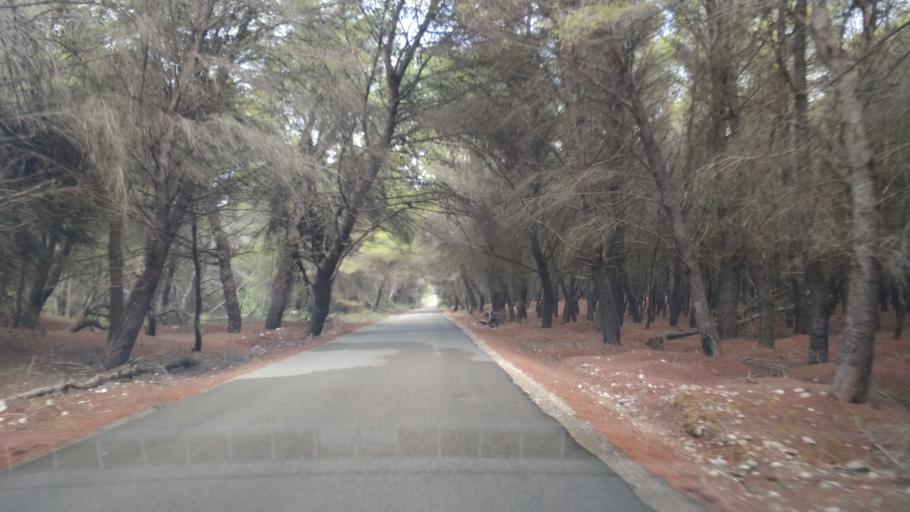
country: AL
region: Vlore
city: Vlore
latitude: 40.4985
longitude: 19.4308
